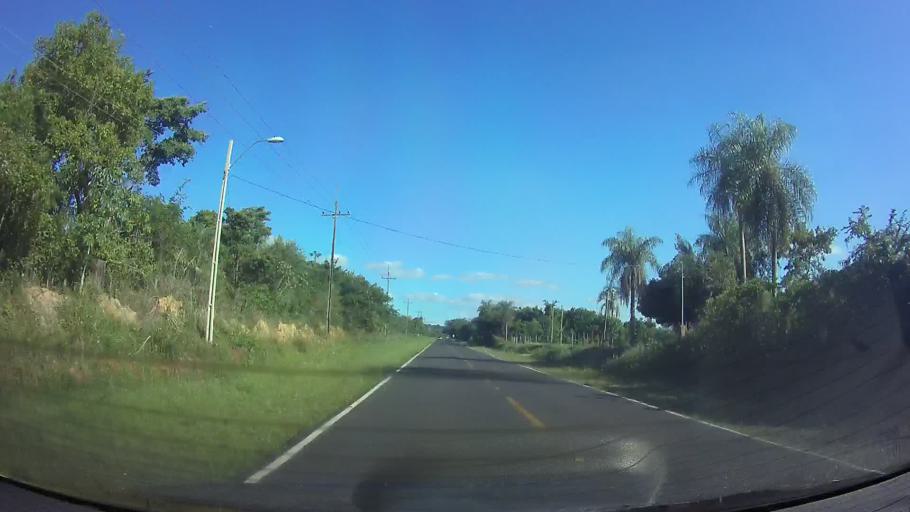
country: PY
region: Cordillera
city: Atyra
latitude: -25.2921
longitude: -57.1664
